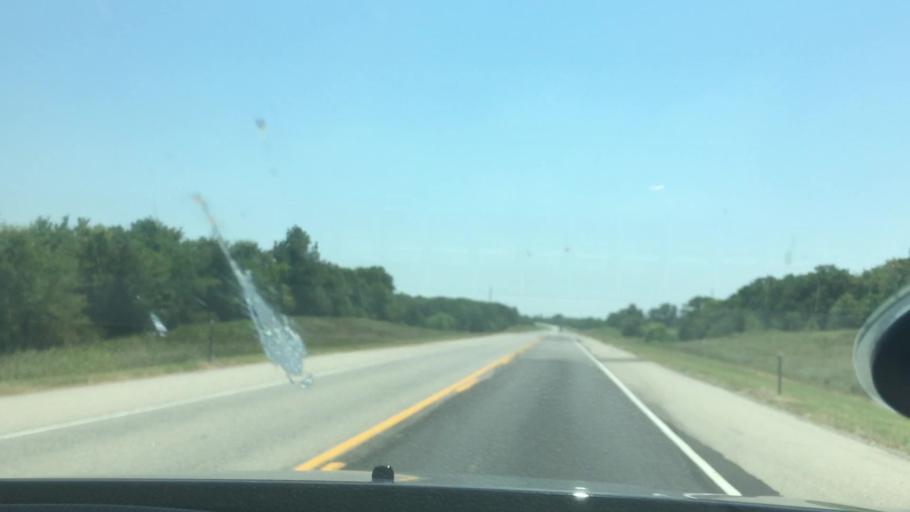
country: US
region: Oklahoma
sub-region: Pontotoc County
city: Ada
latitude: 34.6573
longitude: -96.5589
